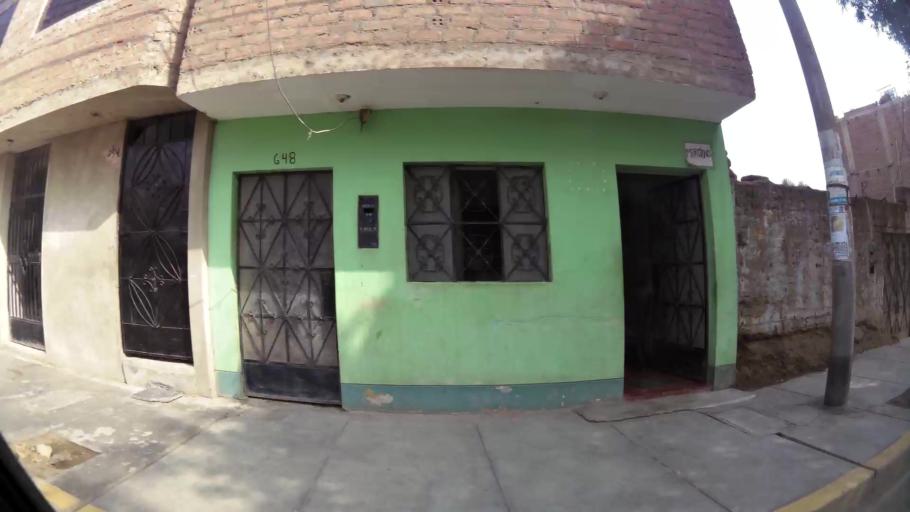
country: PE
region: La Libertad
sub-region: Provincia de Trujillo
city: Trujillo
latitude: -8.1167
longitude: -79.0135
